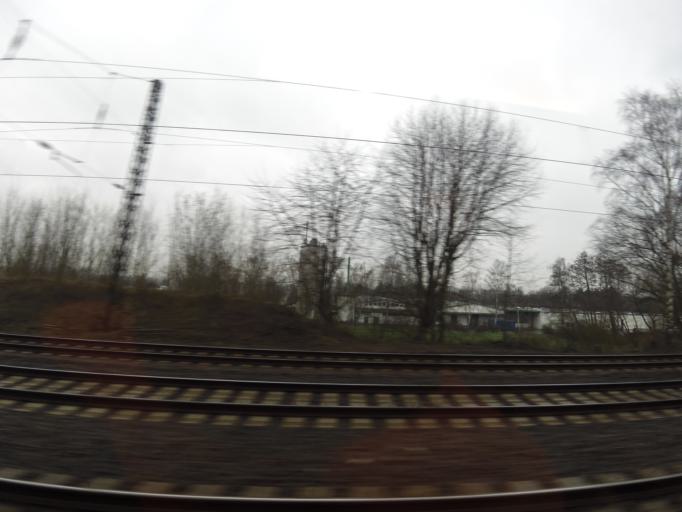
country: DE
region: North Rhine-Westphalia
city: Loehne
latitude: 52.1986
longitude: 8.7420
